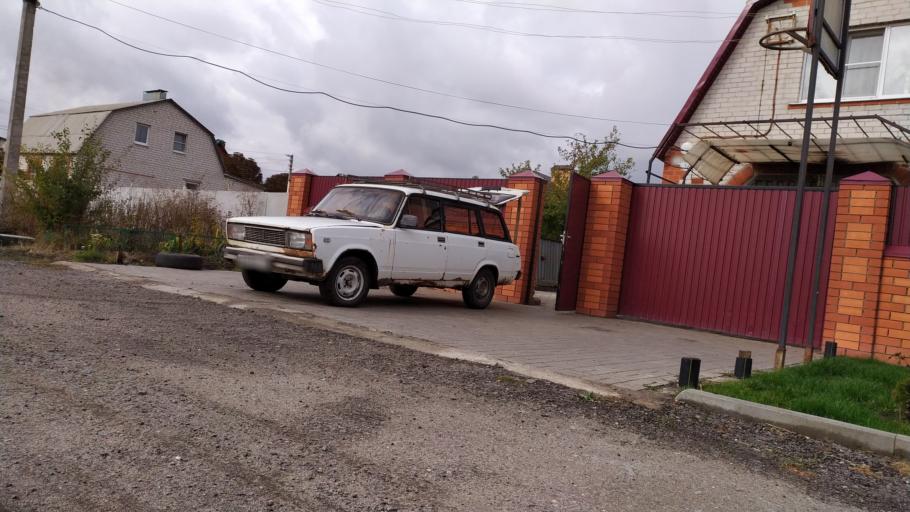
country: RU
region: Kursk
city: Kursk
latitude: 51.6411
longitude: 36.1534
